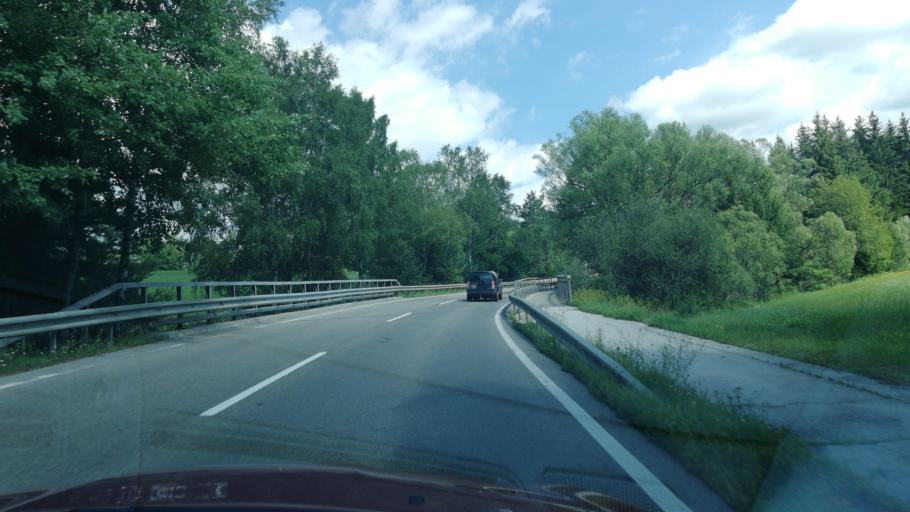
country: AT
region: Styria
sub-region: Politischer Bezirk Murau
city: Sankt Marein bei Neumarkt
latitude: 47.0500
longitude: 14.4324
